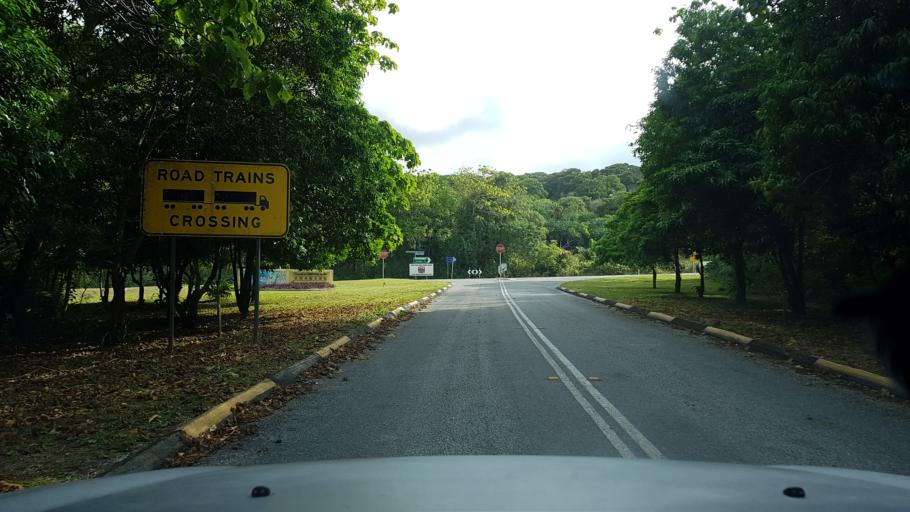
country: CX
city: Flying Fish Cove
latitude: -10.4517
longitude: 105.6877
